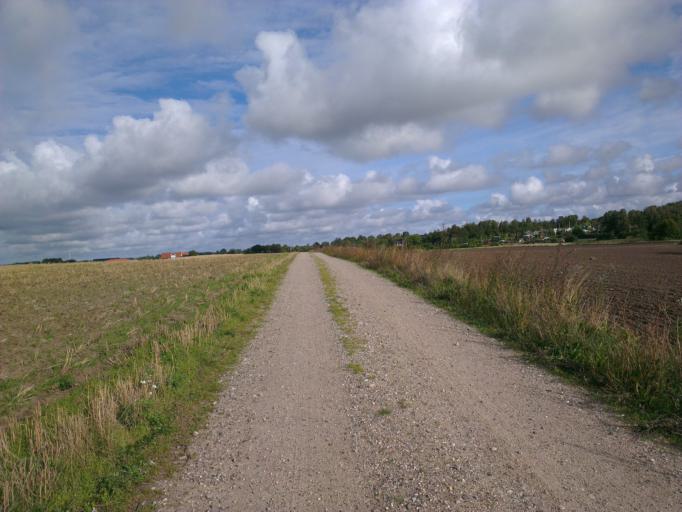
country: DK
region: Capital Region
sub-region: Frederikssund Kommune
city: Frederikssund
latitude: 55.8134
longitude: 12.0875
